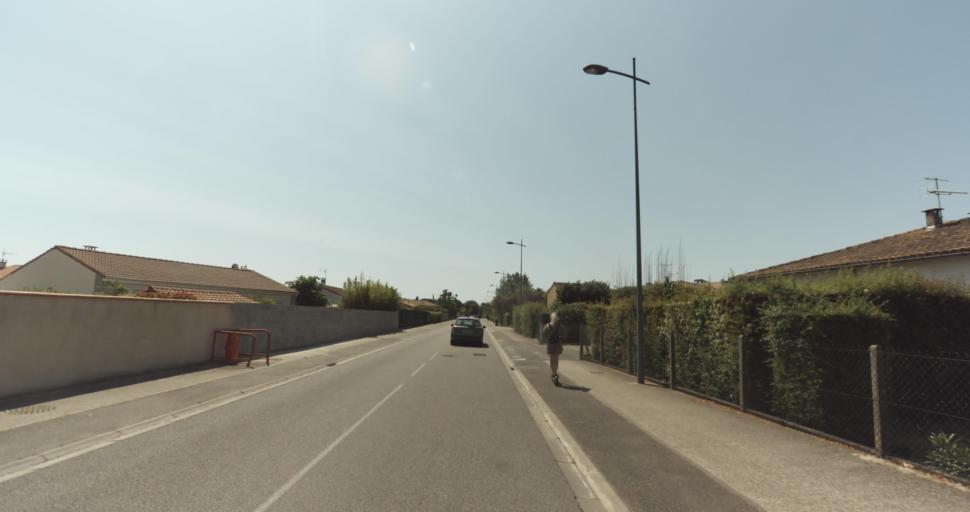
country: FR
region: Midi-Pyrenees
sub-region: Departement de la Haute-Garonne
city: Plaisance-du-Touch
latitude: 43.5780
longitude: 1.2882
